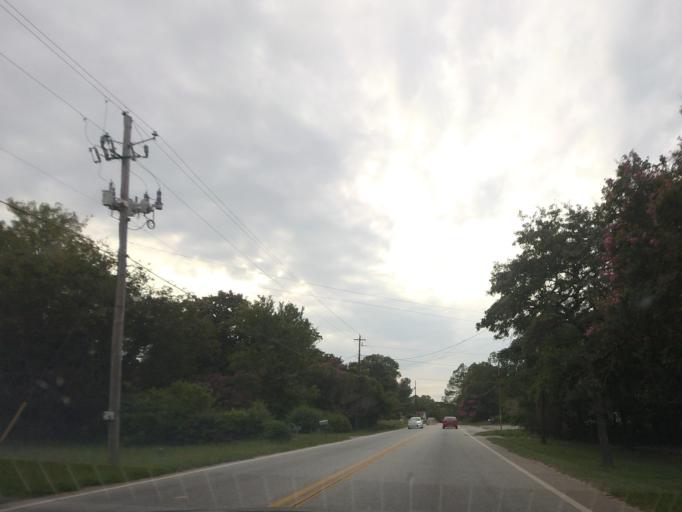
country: US
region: Georgia
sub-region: Bibb County
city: Macon
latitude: 32.8378
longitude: -83.5478
